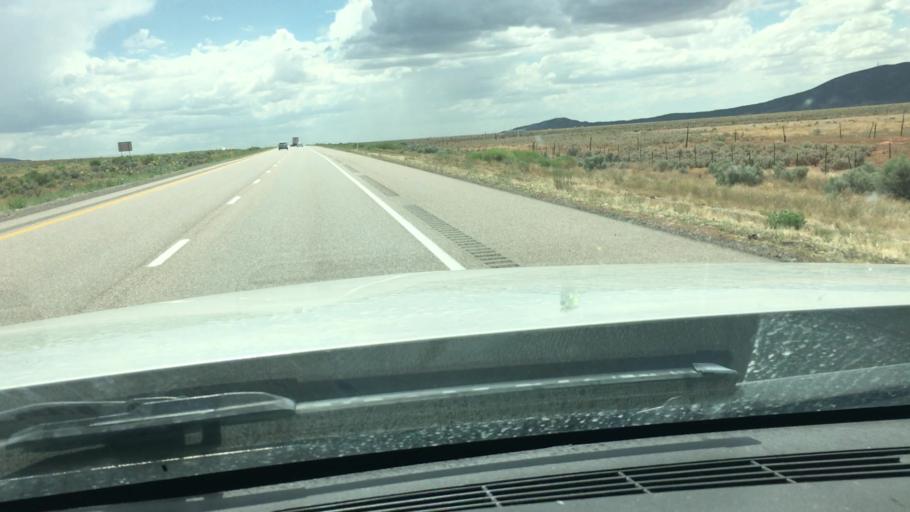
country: US
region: Utah
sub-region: Iron County
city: Parowan
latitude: 37.8316
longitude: -112.8912
